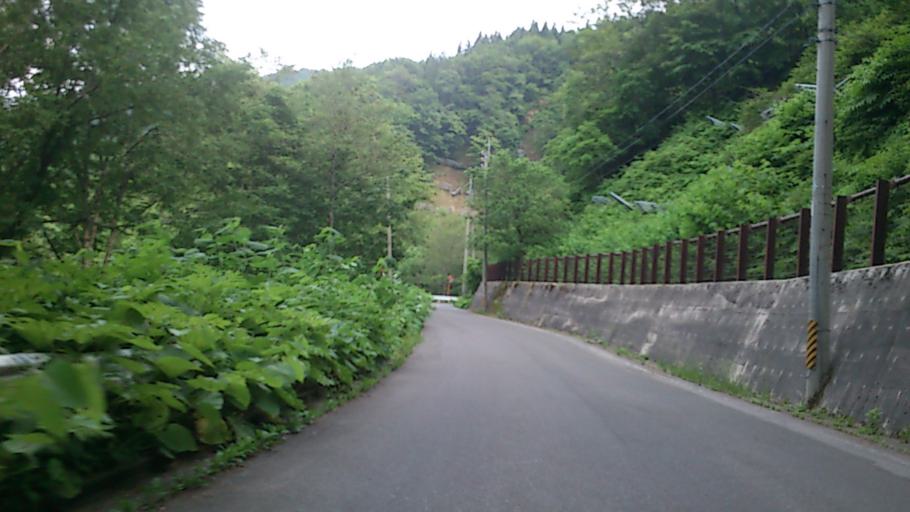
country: JP
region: Aomori
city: Hirosaki
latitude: 40.5181
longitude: 140.1790
